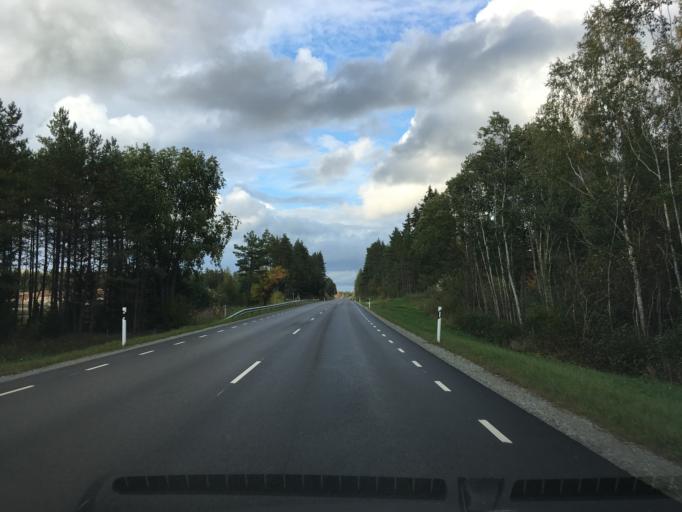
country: EE
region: Harju
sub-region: Nissi vald
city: Turba
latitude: 59.1876
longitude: 24.0891
